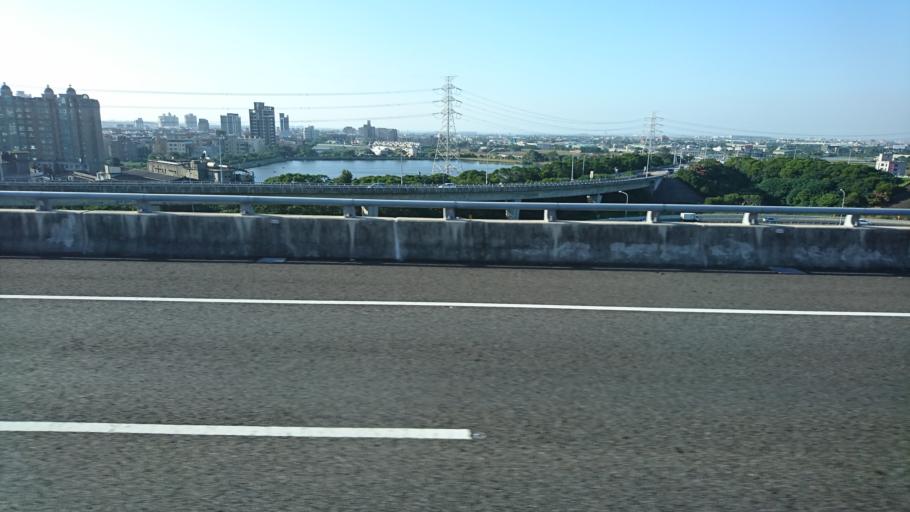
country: TW
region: Taiwan
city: Taoyuan City
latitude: 25.0181
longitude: 121.2719
